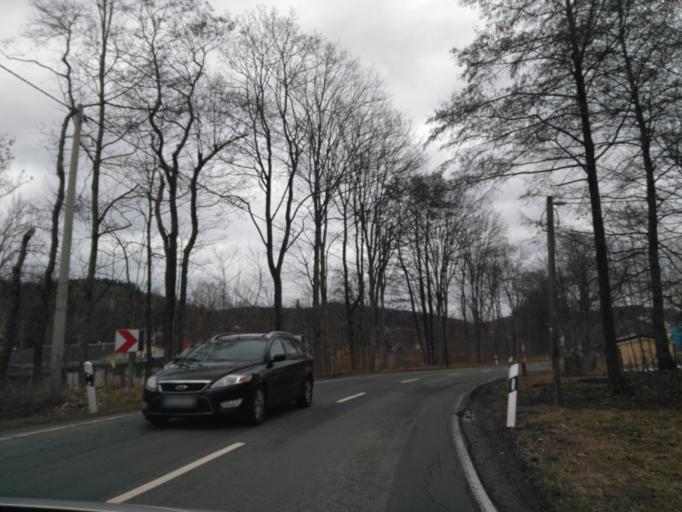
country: DE
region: Saxony
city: Thum
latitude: 50.6695
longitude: 12.9699
